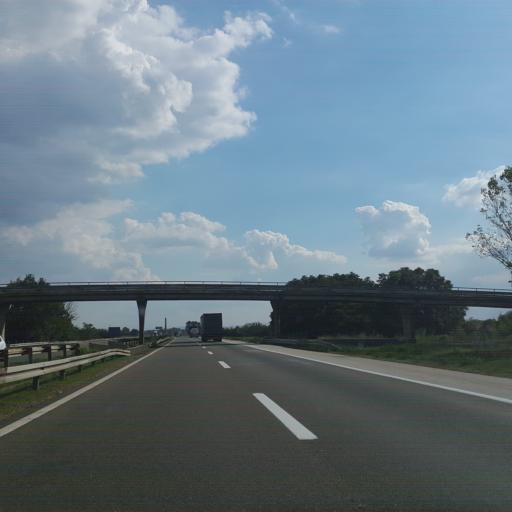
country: RS
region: Central Serbia
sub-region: Podunavski Okrug
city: Velika Plana
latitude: 44.3089
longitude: 21.0937
